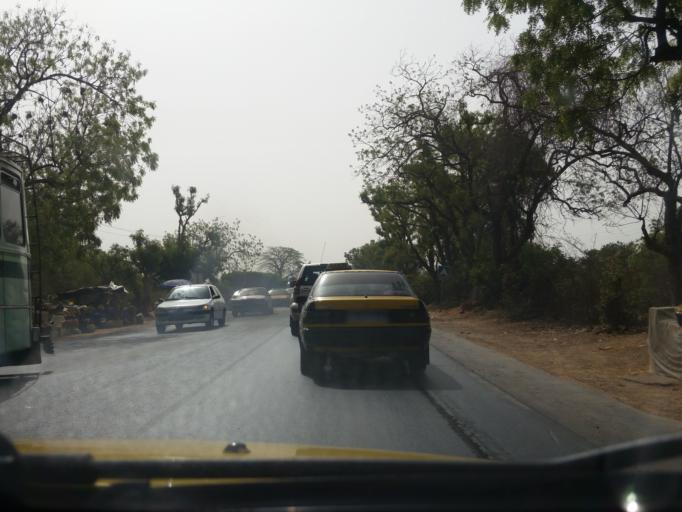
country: SN
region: Thies
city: Pout
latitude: 14.7622
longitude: -17.0413
